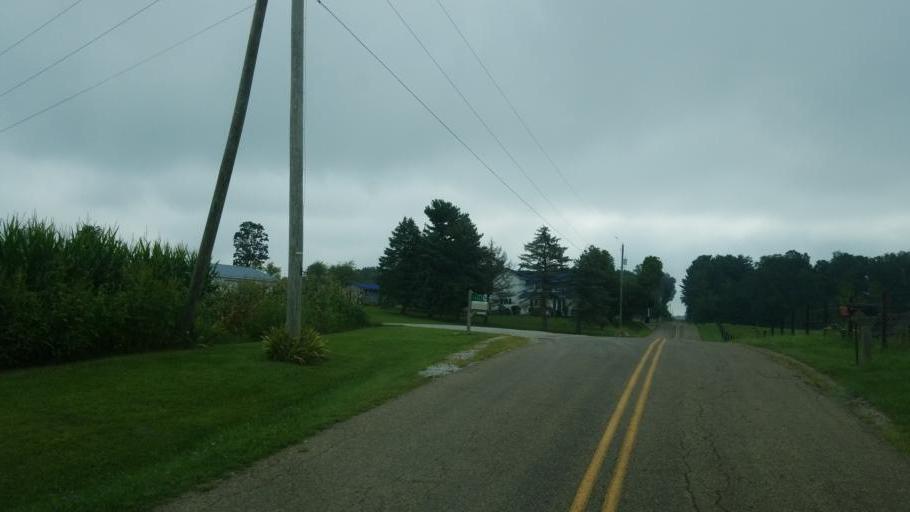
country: US
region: Ohio
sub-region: Licking County
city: Utica
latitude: 40.2799
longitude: -82.4061
